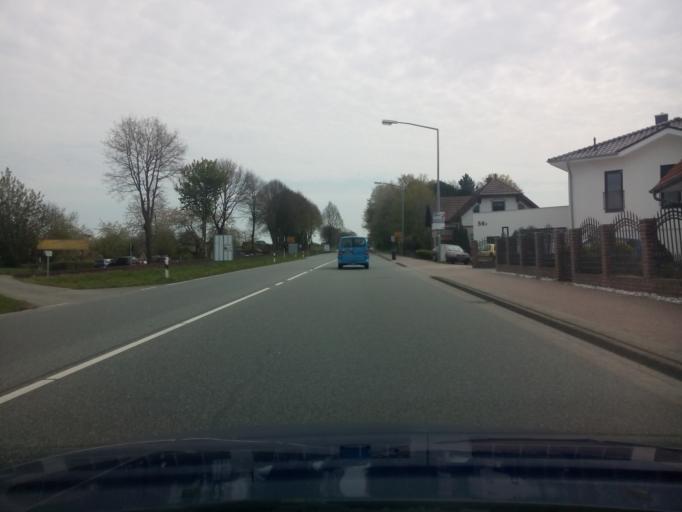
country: DE
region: Lower Saxony
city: Syke
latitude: 52.9080
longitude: 8.8343
